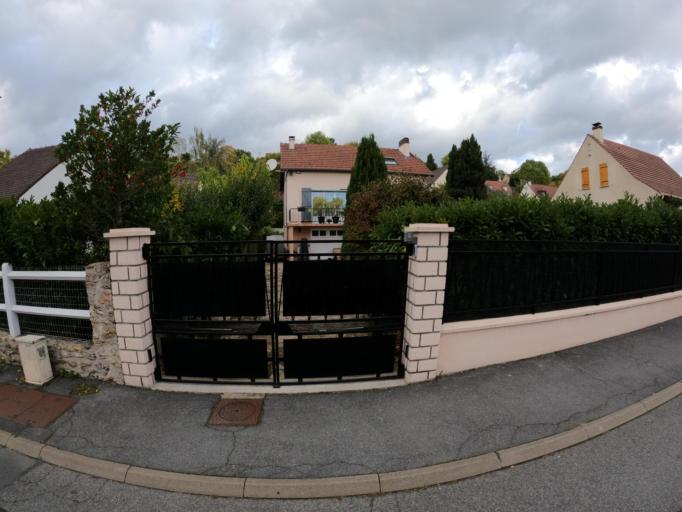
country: FR
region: Ile-de-France
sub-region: Departement de Seine-et-Marne
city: Esbly
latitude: 48.9035
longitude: 2.8013
